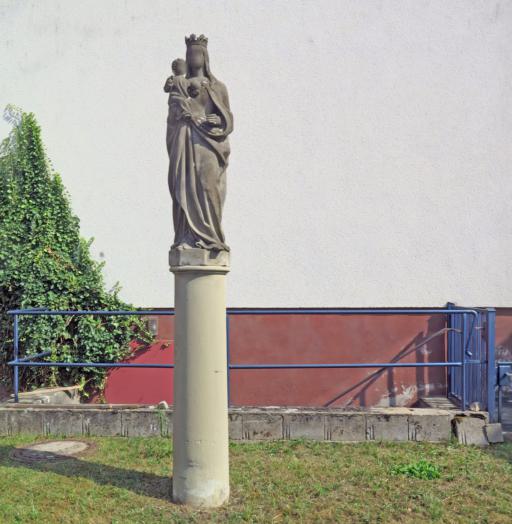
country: DE
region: Bavaria
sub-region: Regierungsbezirk Unterfranken
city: Knetzgau
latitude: 49.9649
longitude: 10.5642
